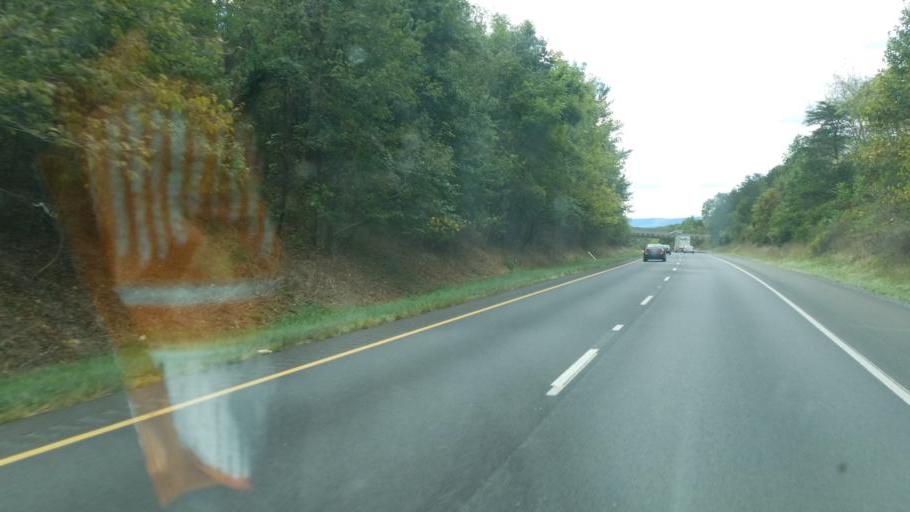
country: US
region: Maryland
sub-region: Washington County
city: Wilson-Conococheague
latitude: 39.6343
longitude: -77.9611
